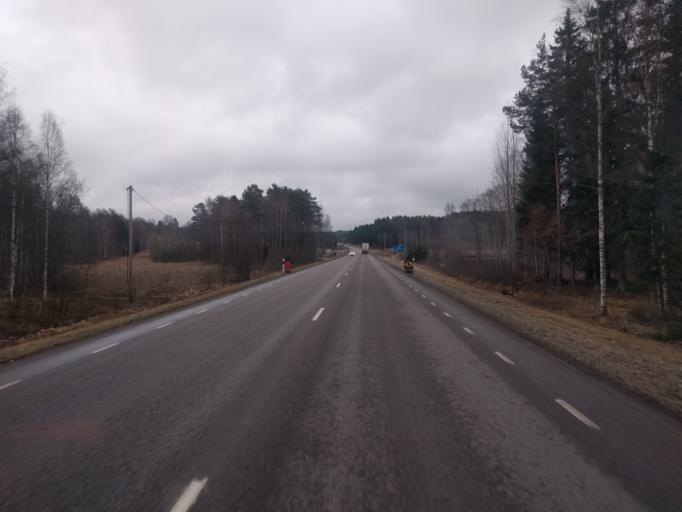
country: SE
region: Joenkoeping
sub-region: Aneby Kommun
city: Aneby
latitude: 57.7925
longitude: 14.8749
